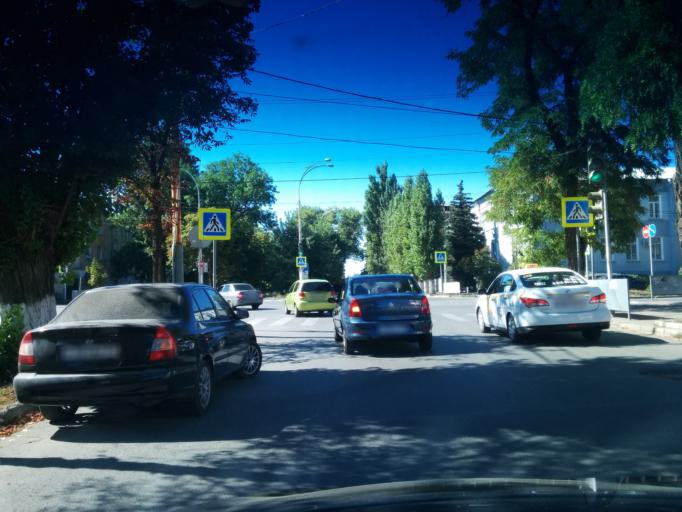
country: RU
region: Rostov
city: Shakhty
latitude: 47.7139
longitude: 40.2109
